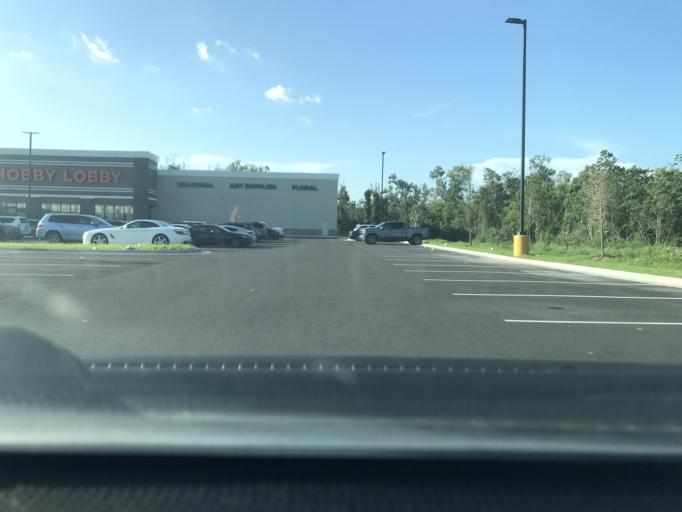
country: US
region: Louisiana
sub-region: Calcasieu Parish
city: Prien
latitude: 30.1989
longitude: -93.2445
